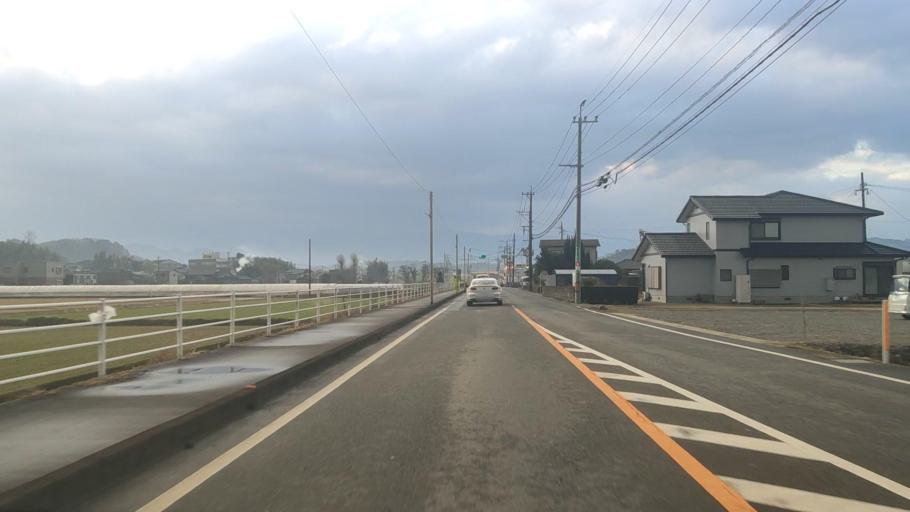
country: JP
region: Kumamoto
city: Uto
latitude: 32.7058
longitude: 130.7774
